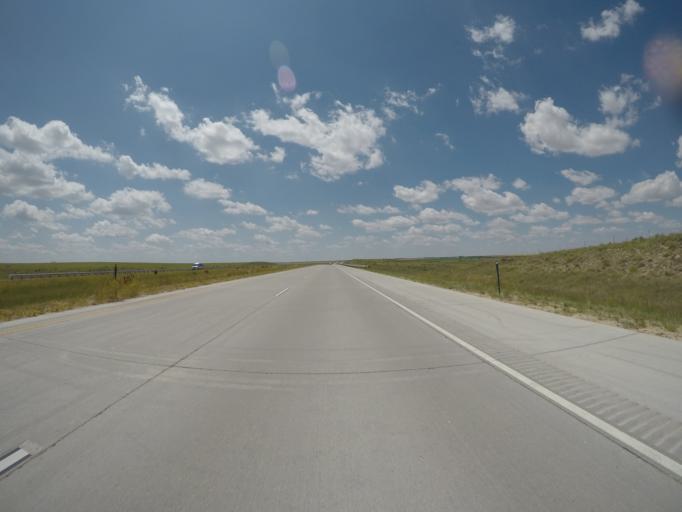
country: US
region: Colorado
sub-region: Kit Carson County
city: Burlington
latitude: 39.2943
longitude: -102.6380
